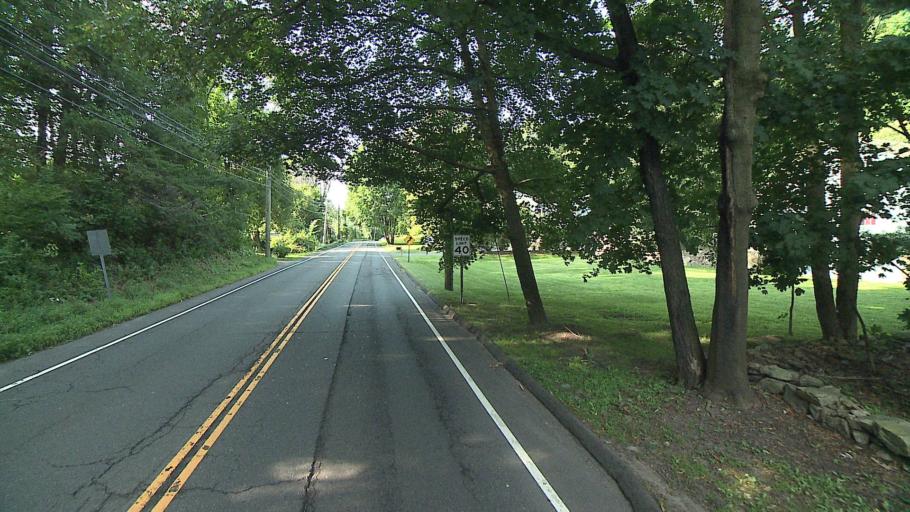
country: US
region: Connecticut
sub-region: Fairfield County
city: Georgetown
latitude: 41.2250
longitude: -73.4257
